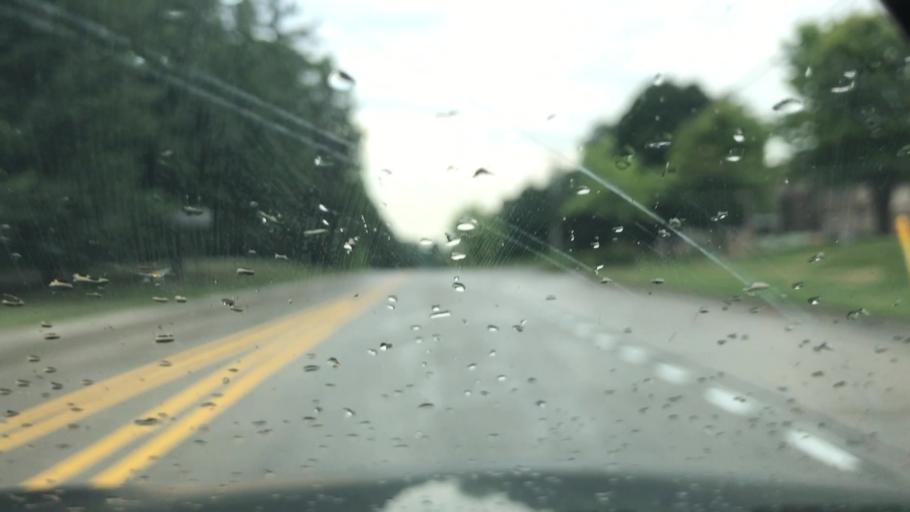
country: US
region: Michigan
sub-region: Oakland County
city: Farmington Hills
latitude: 42.5133
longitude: -83.4181
